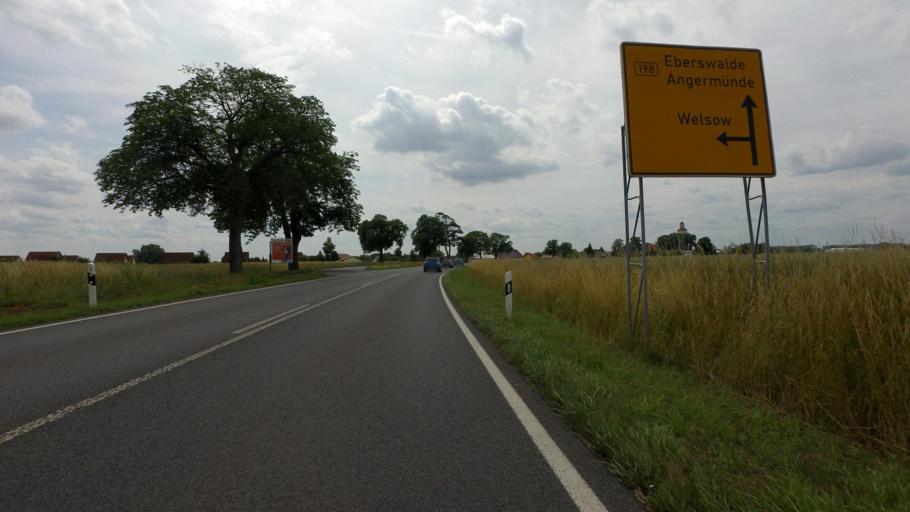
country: DE
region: Brandenburg
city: Angermunde
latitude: 53.0429
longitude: 13.9891
